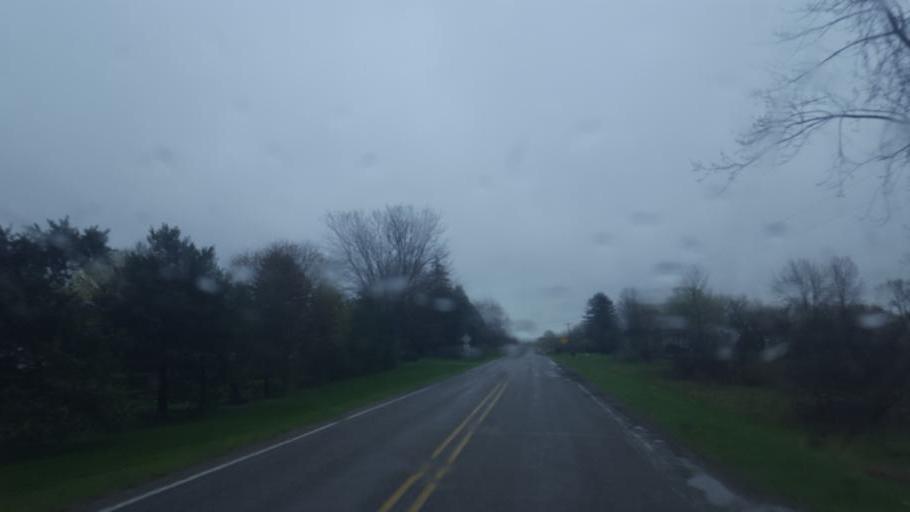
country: US
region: Michigan
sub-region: Isabella County
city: Mount Pleasant
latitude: 43.6122
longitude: -84.8665
